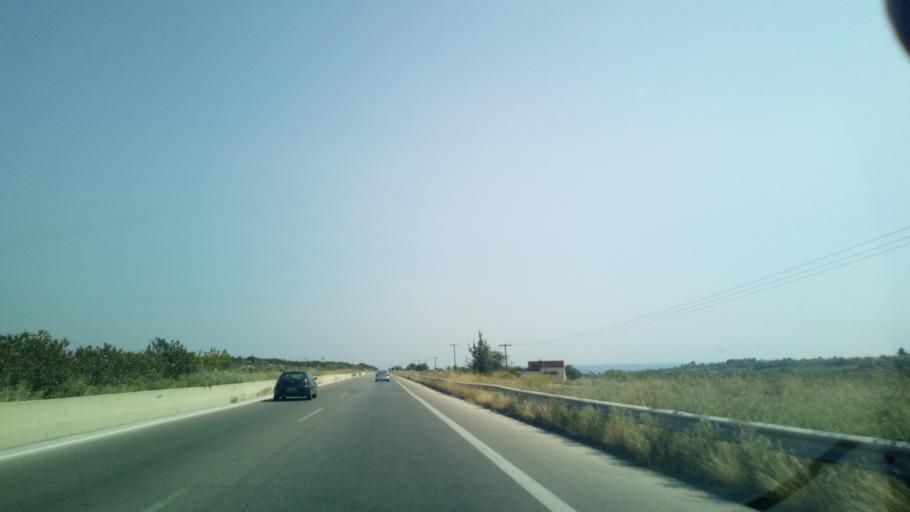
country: GR
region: Central Macedonia
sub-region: Nomos Chalkidikis
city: Nea Kallikrateia
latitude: 40.3277
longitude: 23.0792
